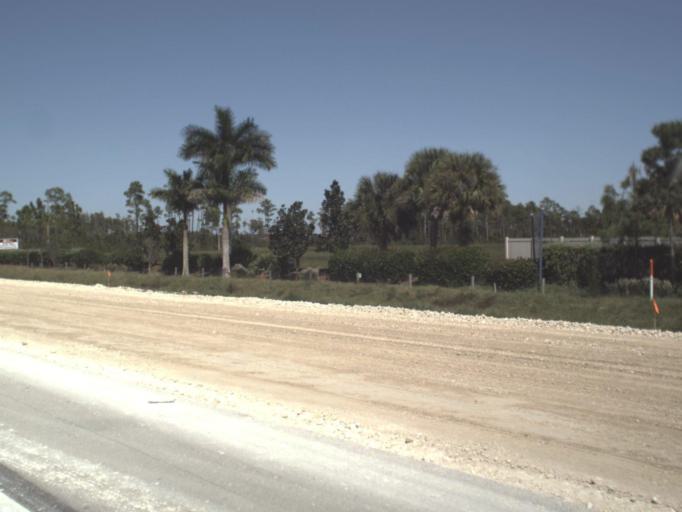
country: US
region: Florida
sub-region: Lee County
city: Three Oaks
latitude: 26.5261
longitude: -81.7946
